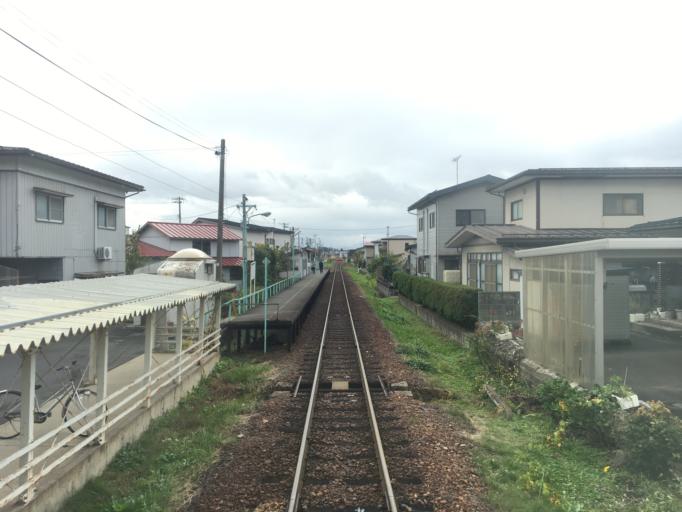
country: JP
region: Yamagata
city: Nagai
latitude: 38.0981
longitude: 140.0345
